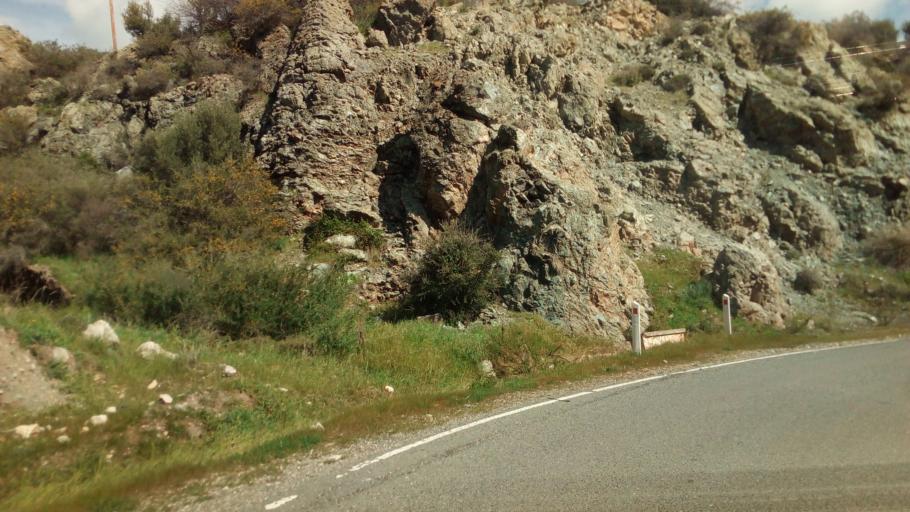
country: CY
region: Pafos
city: Mesogi
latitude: 34.7619
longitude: 32.5524
